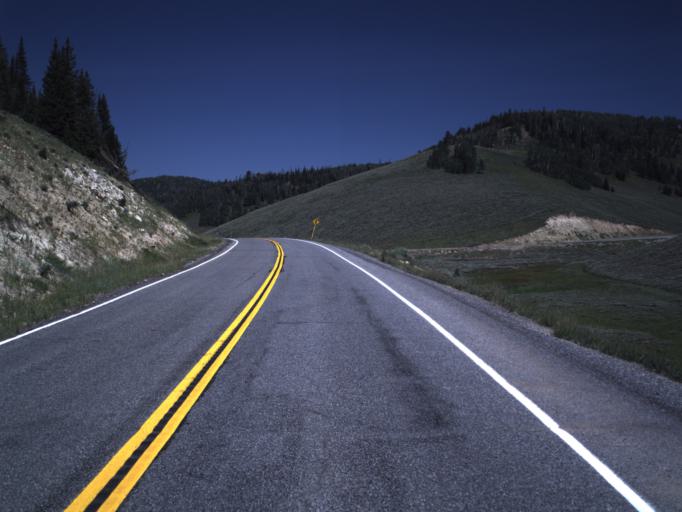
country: US
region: Utah
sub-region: Sanpete County
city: Fairview
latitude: 39.6825
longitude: -111.2448
